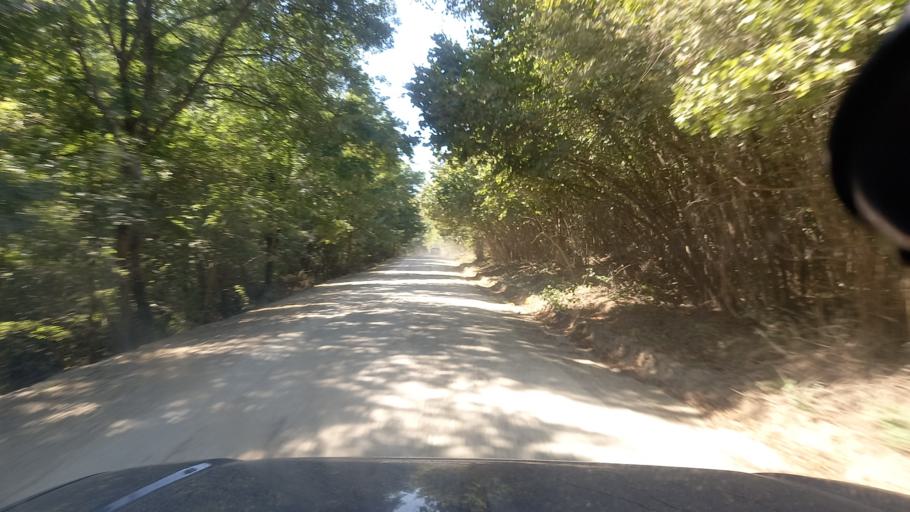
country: RU
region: Krasnodarskiy
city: Azovskaya
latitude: 44.6968
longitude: 38.6475
